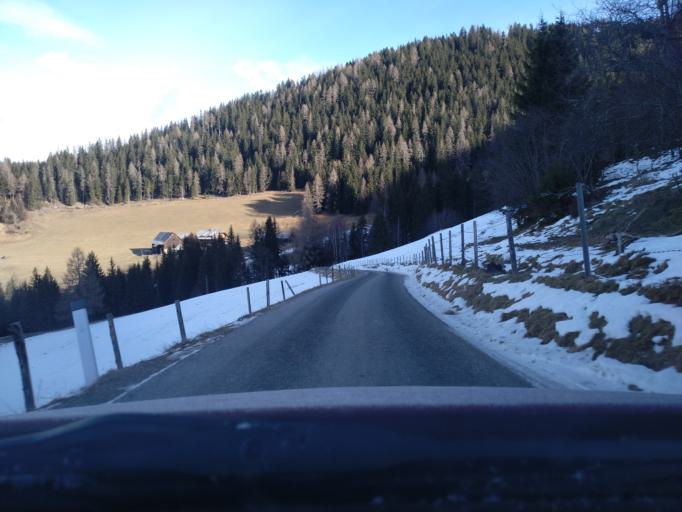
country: AT
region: Carinthia
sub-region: Politischer Bezirk Villach Land
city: Arriach
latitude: 46.7132
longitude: 13.8912
